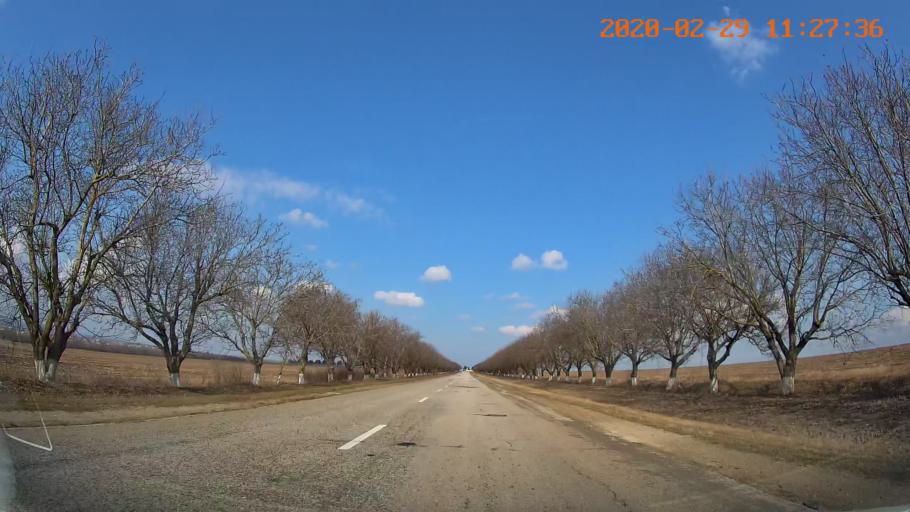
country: MD
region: Telenesti
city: Cocieri
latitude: 47.4708
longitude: 29.1418
